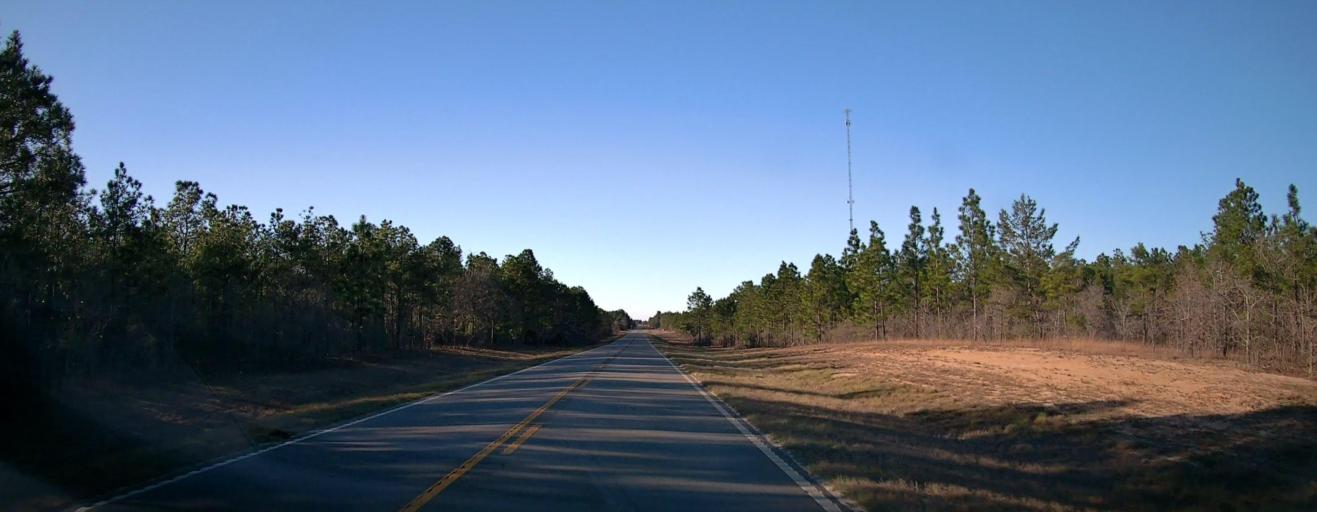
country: US
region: Georgia
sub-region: Talbot County
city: Talbotton
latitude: 32.5677
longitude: -84.4398
